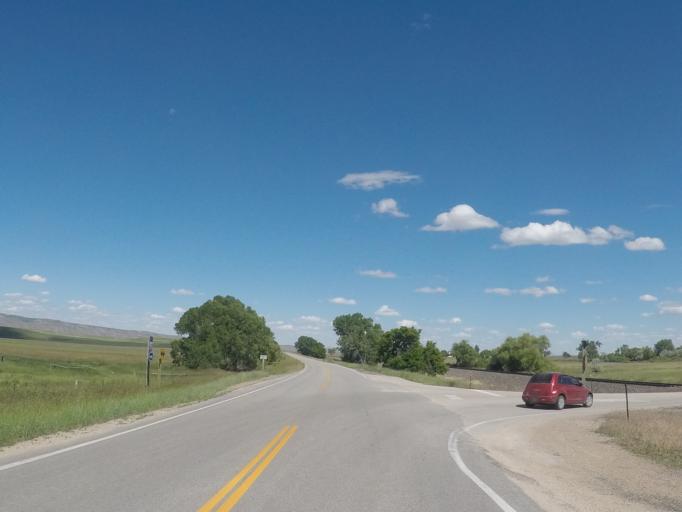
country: US
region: Wyoming
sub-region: Sheridan County
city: Sheridan
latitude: 44.9387
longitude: -107.2862
